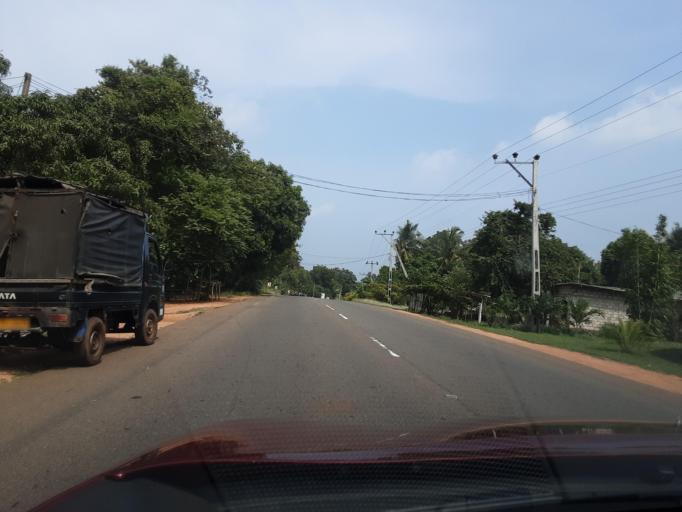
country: LK
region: North Central
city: Anuradhapura
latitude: 8.3339
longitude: 80.5011
